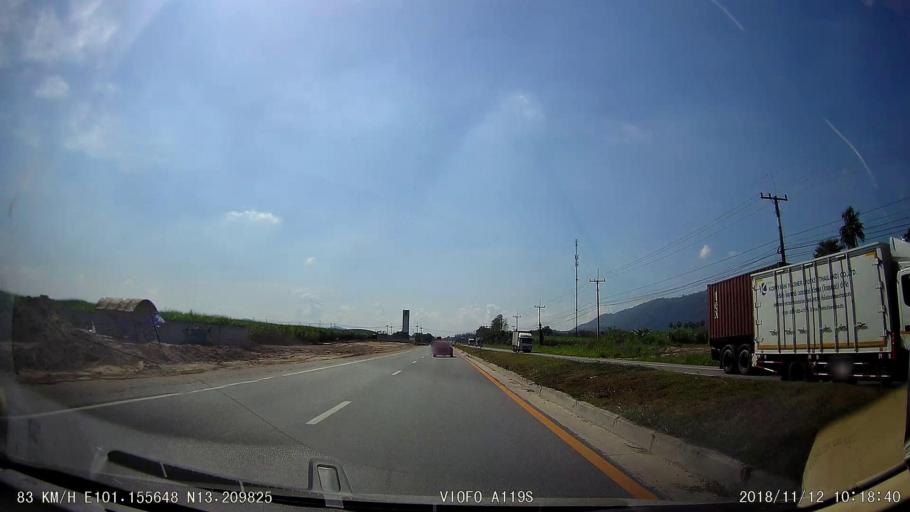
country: TH
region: Chon Buri
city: Ban Bueng
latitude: 13.2093
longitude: 101.1558
